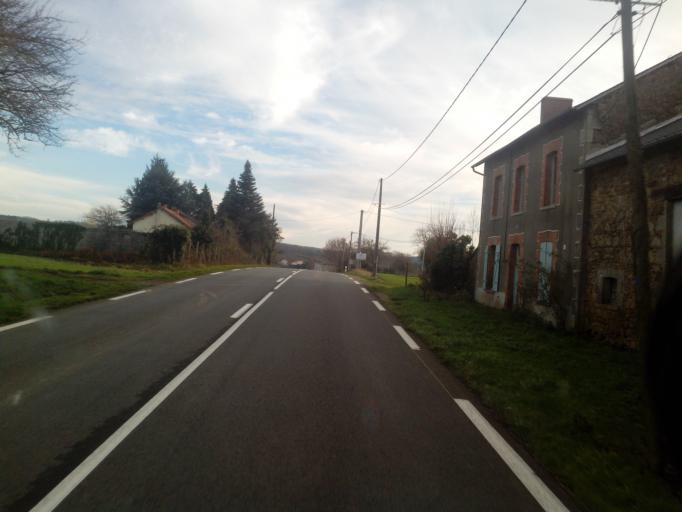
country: FR
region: Limousin
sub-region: Departement de la Haute-Vienne
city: Neuvic-Entier
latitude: 45.7383
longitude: 1.6099
